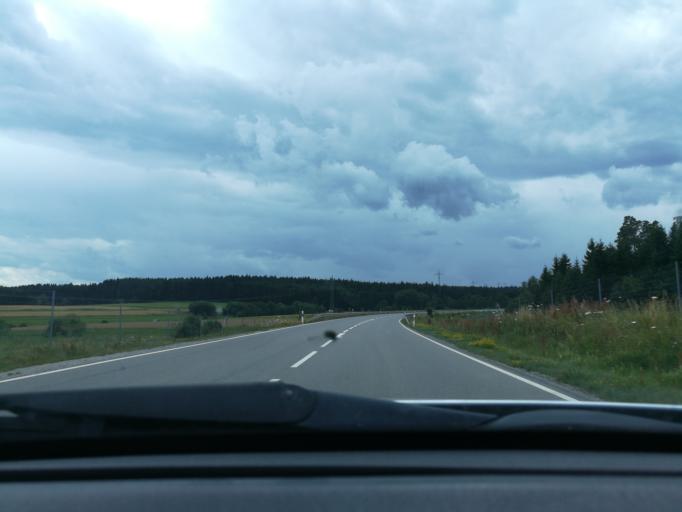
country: DE
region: Baden-Wuerttemberg
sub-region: Freiburg Region
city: Dunningen
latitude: 48.2202
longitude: 8.4823
